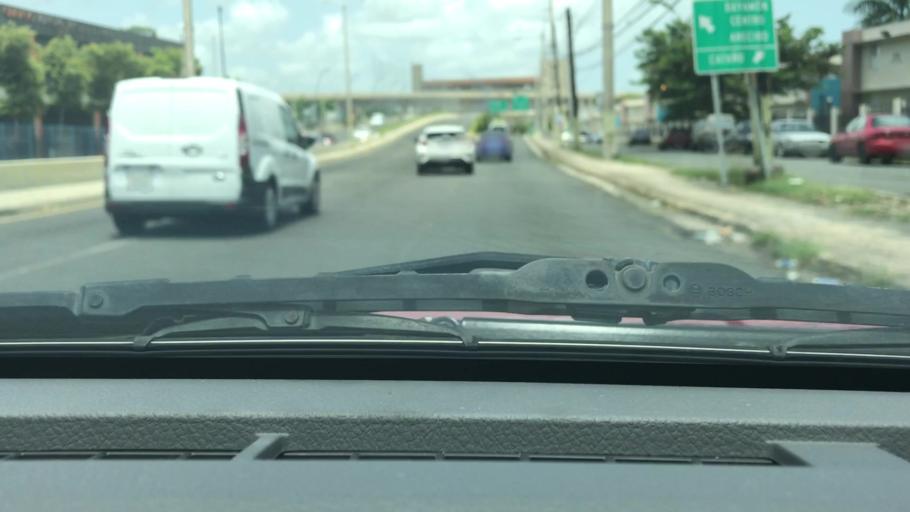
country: PR
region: Bayamon
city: Bayamon
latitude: 18.3959
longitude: -66.1508
